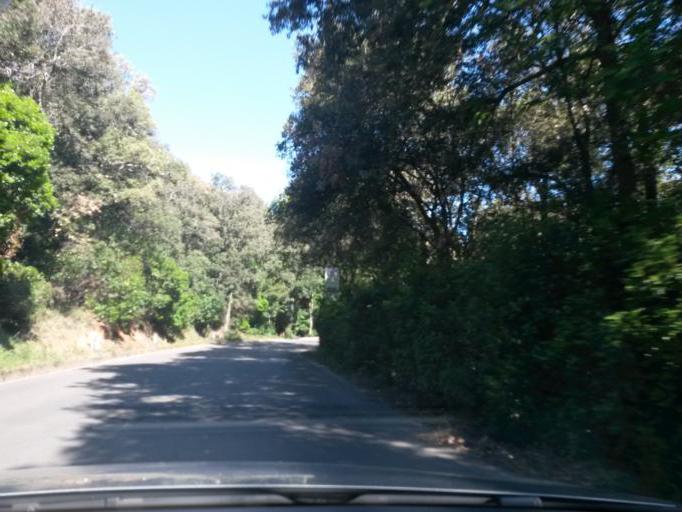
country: IT
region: Tuscany
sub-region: Provincia di Livorno
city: Campo nell'Elba
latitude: 42.7858
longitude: 10.2344
